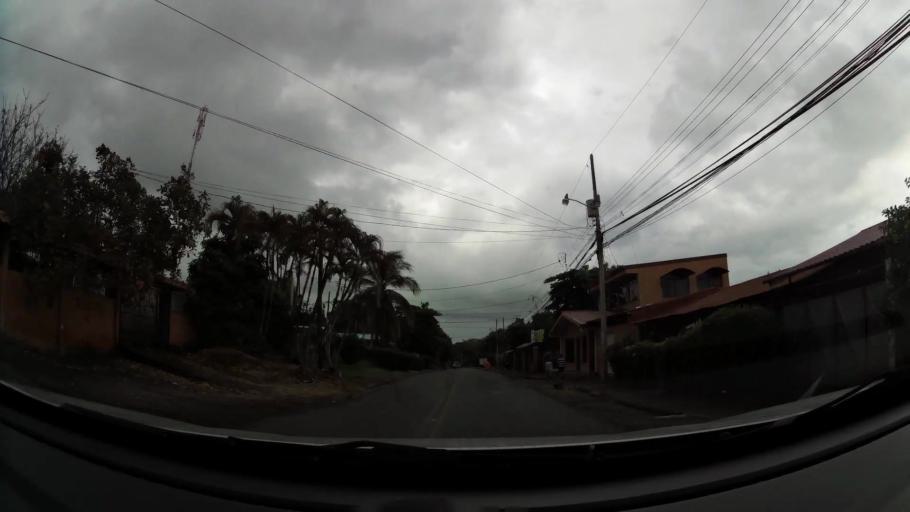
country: CR
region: Puntarenas
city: Esparza
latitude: 9.9958
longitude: -84.6573
